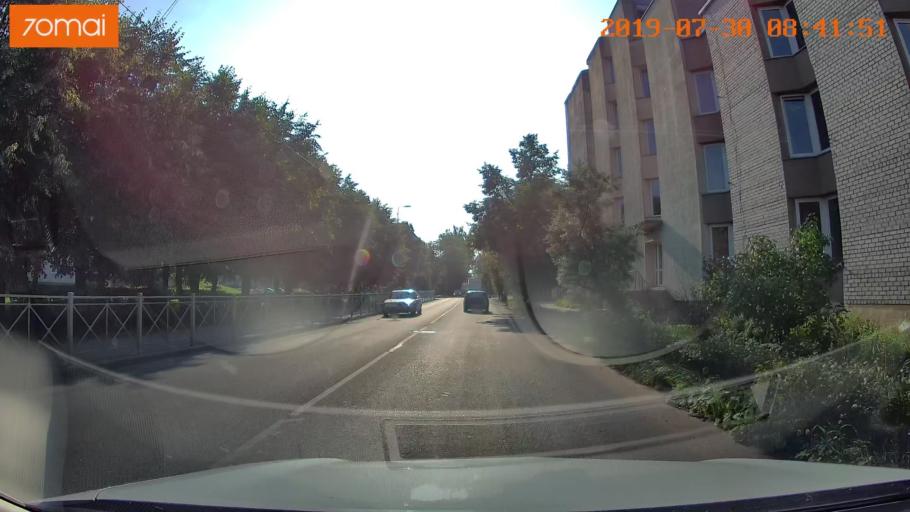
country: RU
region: Kaliningrad
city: Chernyakhovsk
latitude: 54.6300
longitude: 21.8212
